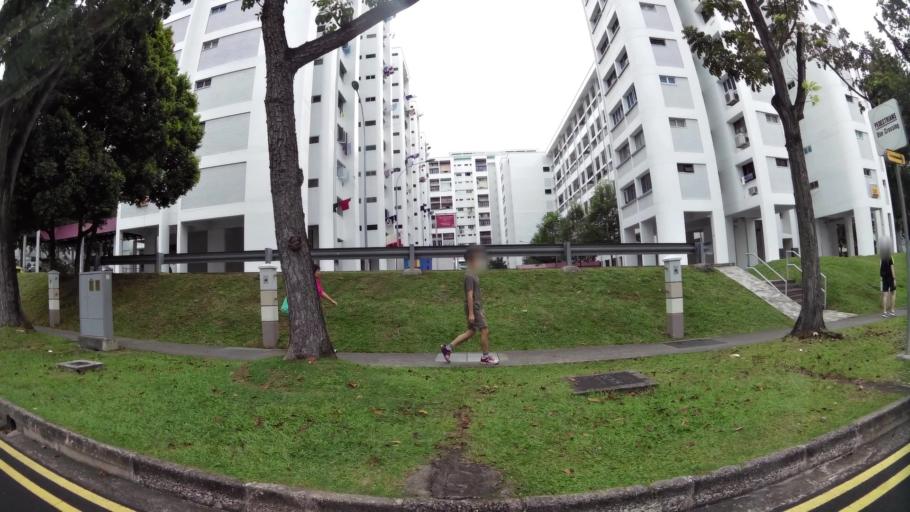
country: SG
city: Singapore
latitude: 1.3590
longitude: 103.8890
